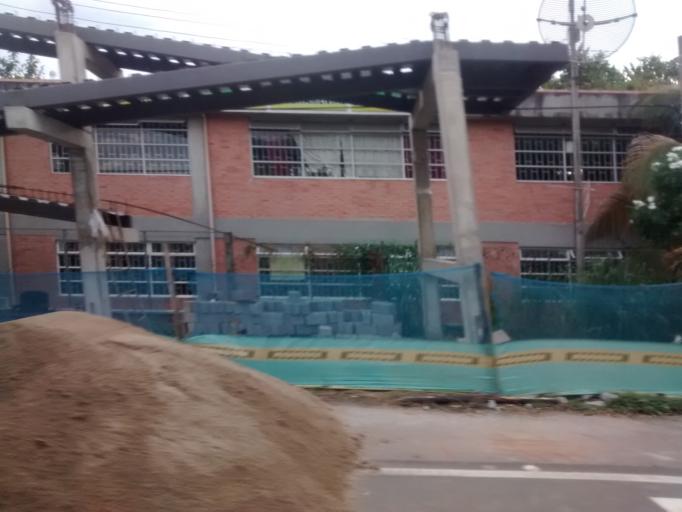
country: CO
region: Tolima
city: Melgar
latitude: 4.2241
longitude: -74.6966
